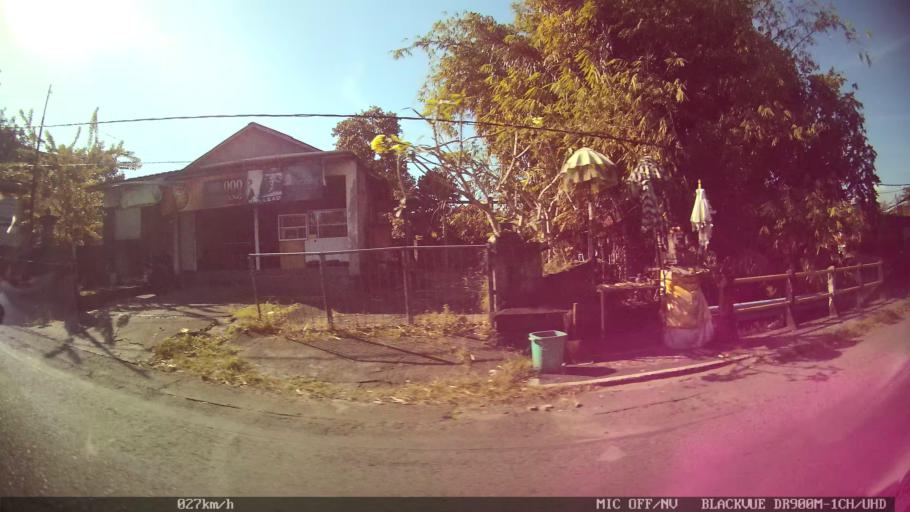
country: ID
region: Bali
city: Banjar Karangsuling
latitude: -8.6200
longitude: 115.1865
